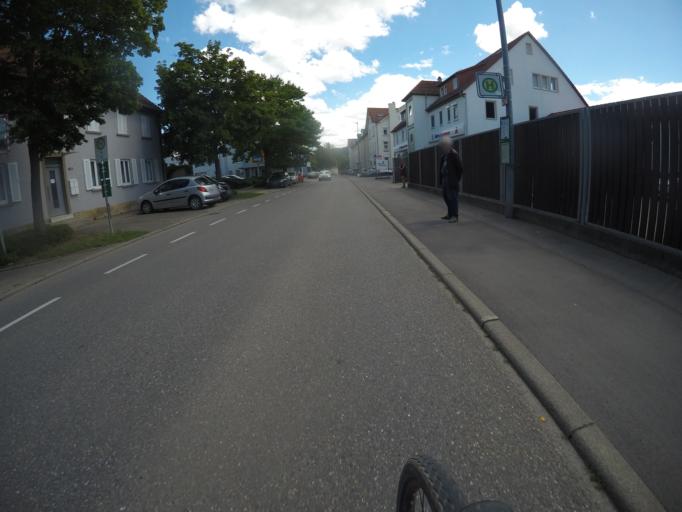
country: DE
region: Baden-Wuerttemberg
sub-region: Tuebingen Region
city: Rottenburg
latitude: 48.4732
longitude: 8.9457
